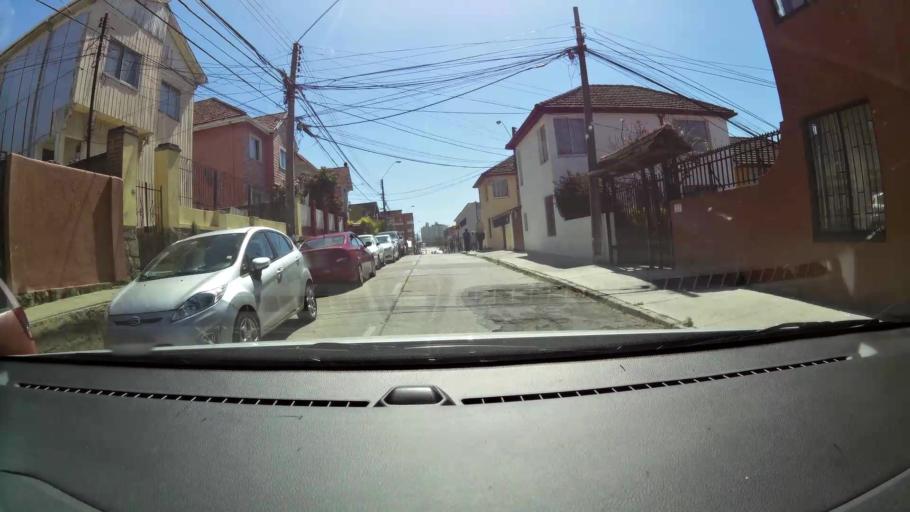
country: CL
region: Valparaiso
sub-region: Provincia de Valparaiso
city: Valparaiso
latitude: -33.0238
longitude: -71.6357
